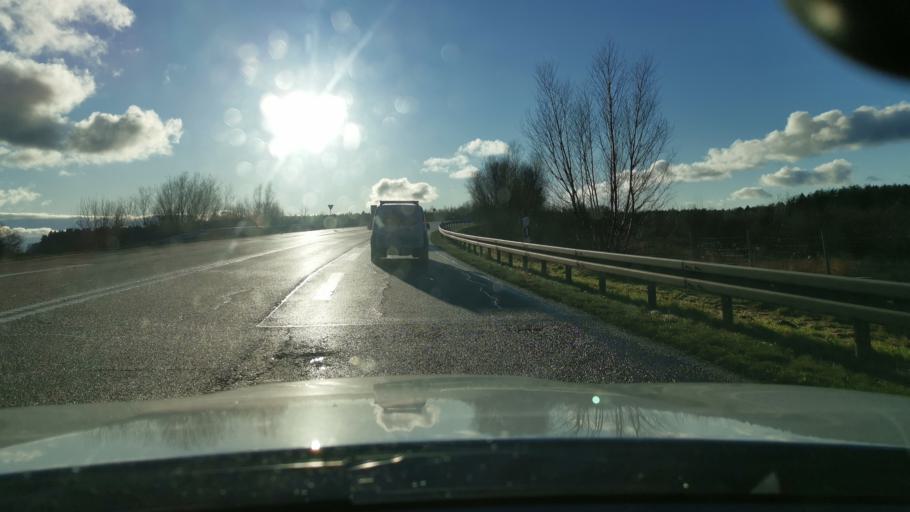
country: DE
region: Mecklenburg-Vorpommern
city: Tessin
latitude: 54.0342
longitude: 12.4116
